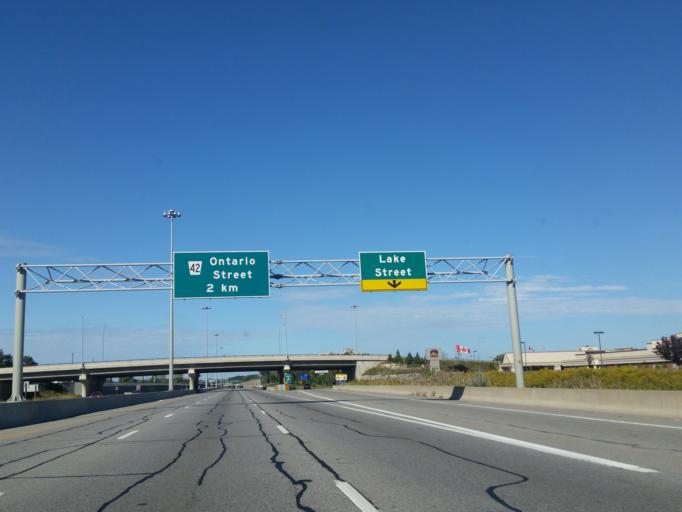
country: CA
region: Ontario
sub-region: Regional Municipality of Niagara
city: St. Catharines
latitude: 43.1767
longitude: -79.2488
